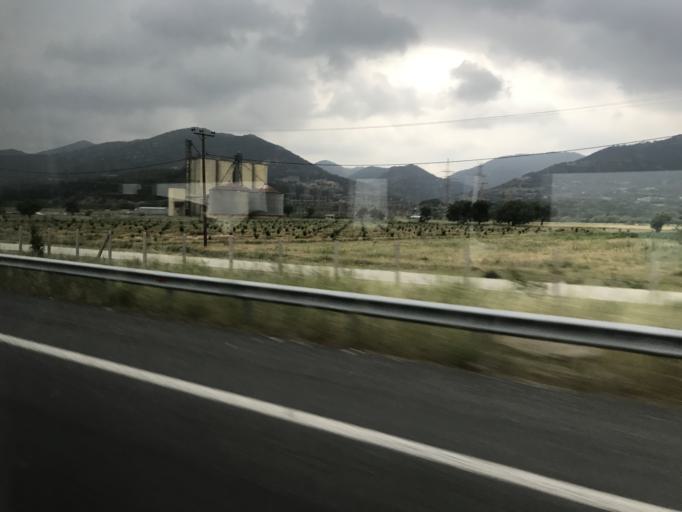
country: GR
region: East Macedonia and Thrace
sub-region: Nomos Rodopis
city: Iasmos
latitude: 41.1166
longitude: 25.1751
